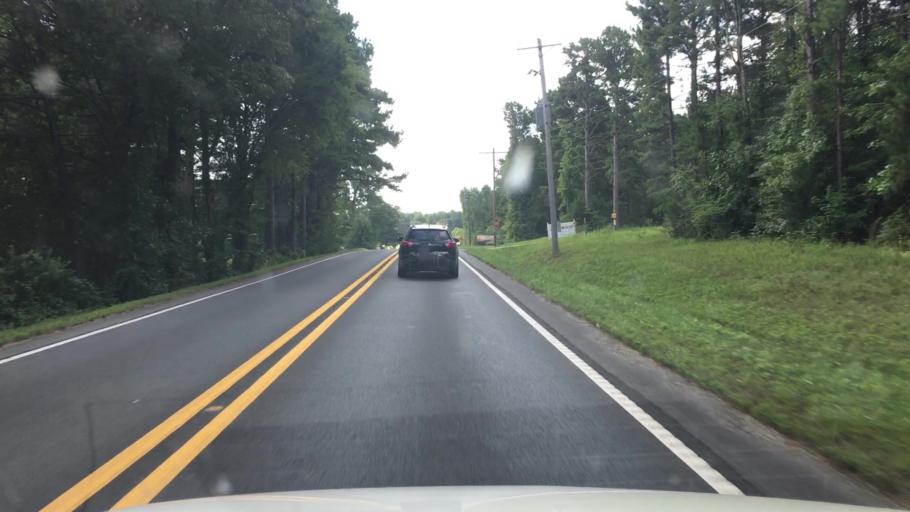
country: US
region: Arkansas
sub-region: Garland County
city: Lake Hamilton
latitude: 34.2711
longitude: -93.1468
